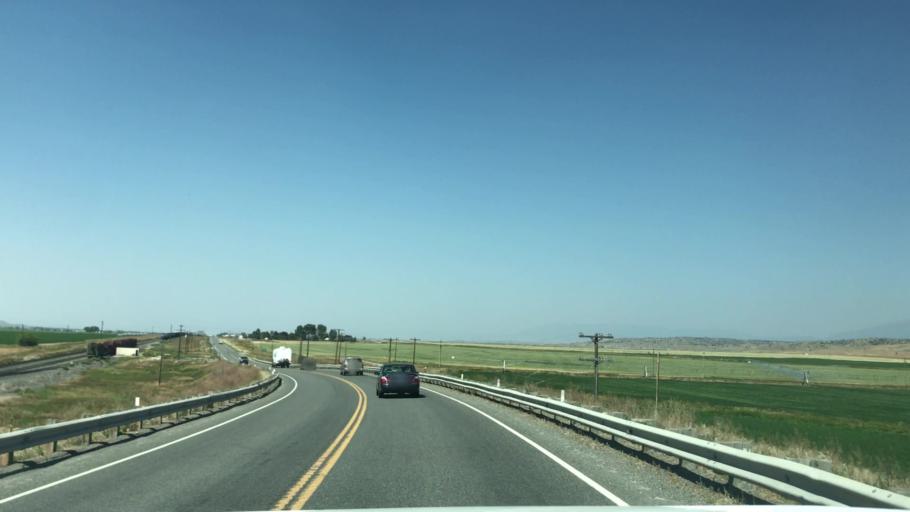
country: US
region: Montana
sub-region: Broadwater County
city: Townsend
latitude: 46.1782
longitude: -111.4437
